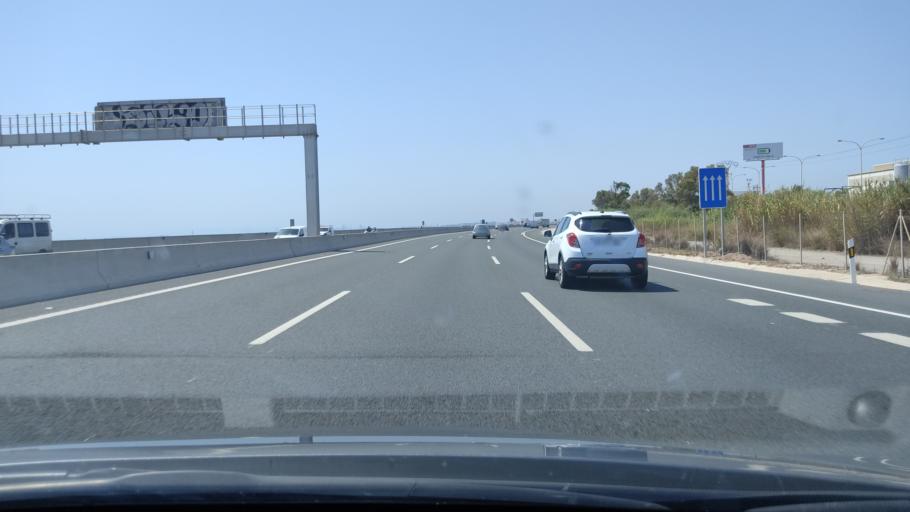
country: ES
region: Valencia
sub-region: Provincia de Valencia
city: Albuixech
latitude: 39.5474
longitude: -0.2986
